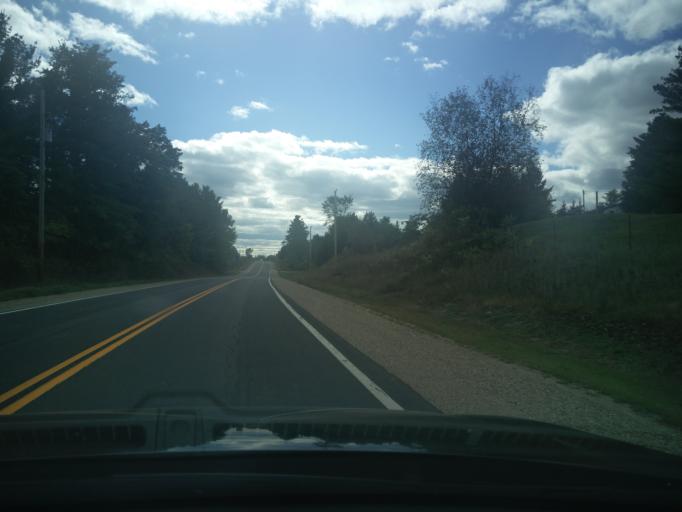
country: CA
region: Ontario
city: Perth
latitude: 44.7904
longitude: -76.3424
